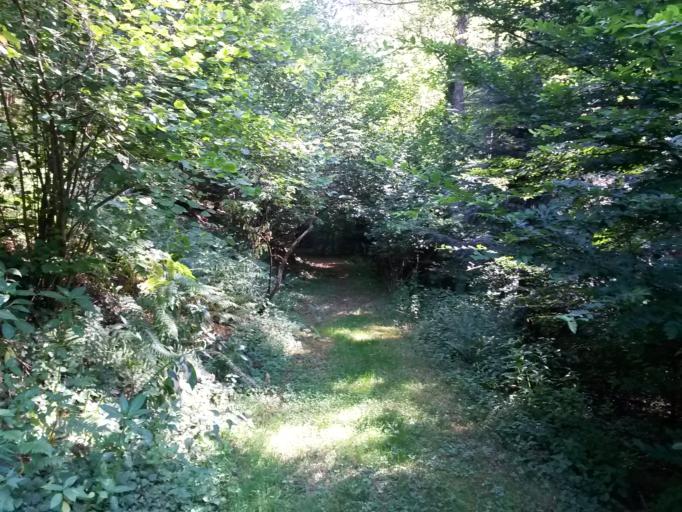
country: DE
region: Baden-Wuerttemberg
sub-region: Karlsruhe Region
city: Buhlertal
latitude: 48.7159
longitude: 8.2030
